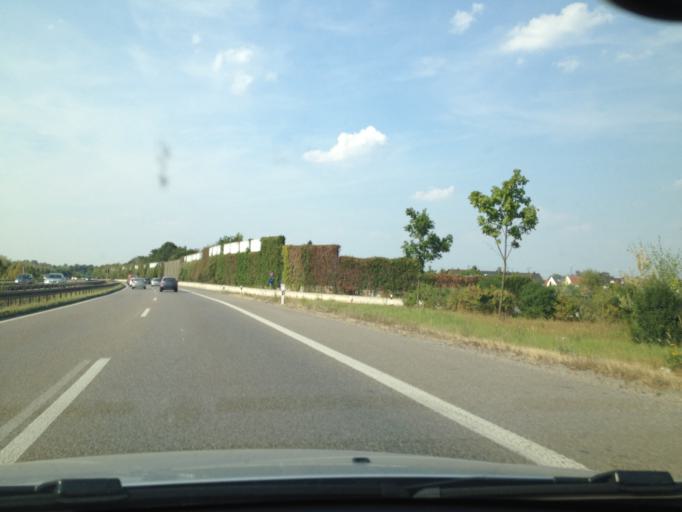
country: DE
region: Bavaria
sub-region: Swabia
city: Gersthofen
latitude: 48.4436
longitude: 10.8727
